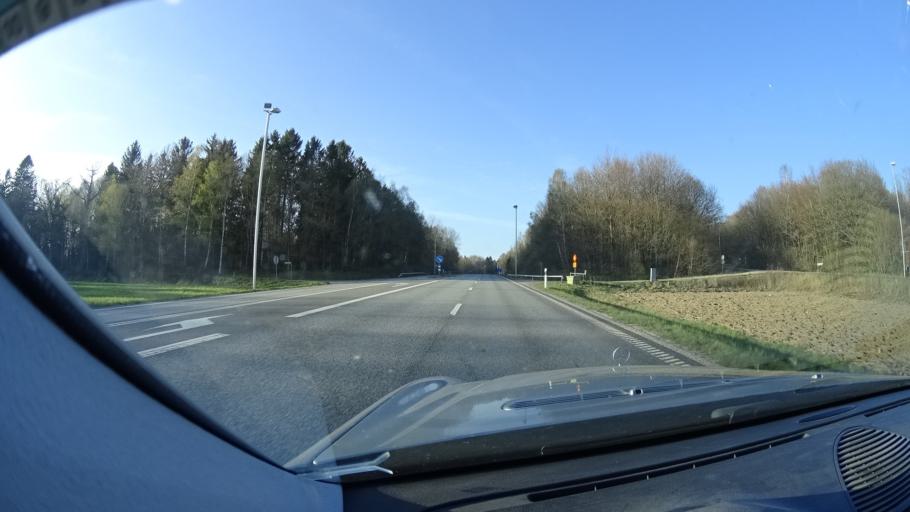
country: SE
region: Skane
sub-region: Hoors Kommun
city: Satofta
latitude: 55.9070
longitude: 13.5220
